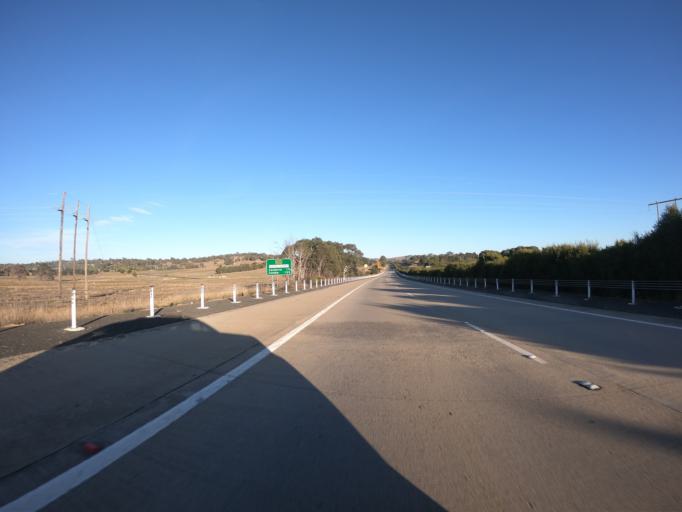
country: AU
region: New South Wales
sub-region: Yass Valley
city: Gundaroo
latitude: -35.1821
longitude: 149.2535
